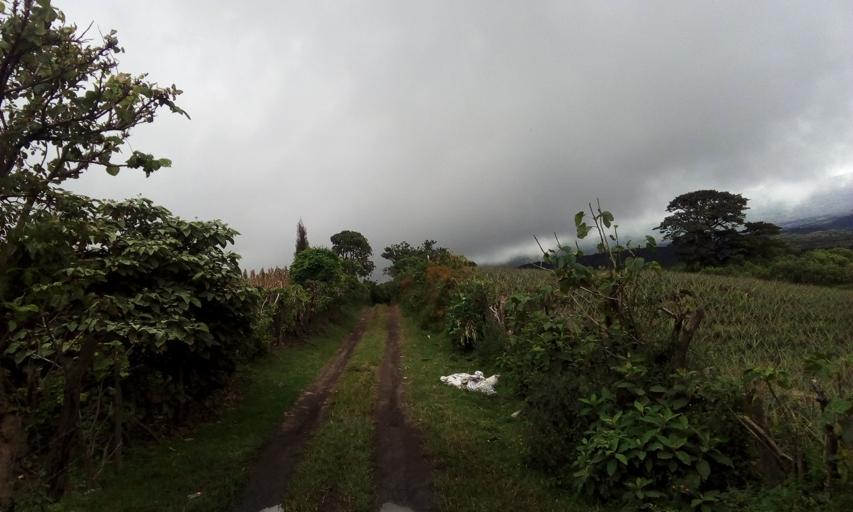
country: GT
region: Escuintla
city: San Vicente Pacaya
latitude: 14.3375
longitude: -90.6136
